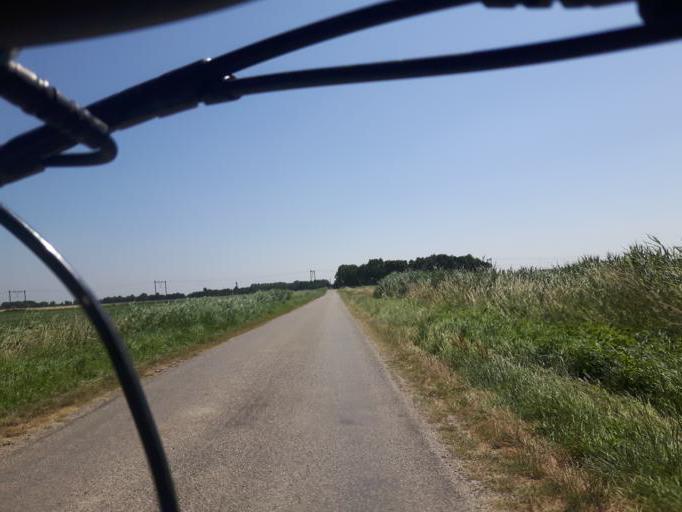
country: NL
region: Zeeland
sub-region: Gemeente Borsele
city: Borssele
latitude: 51.5031
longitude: 3.7798
